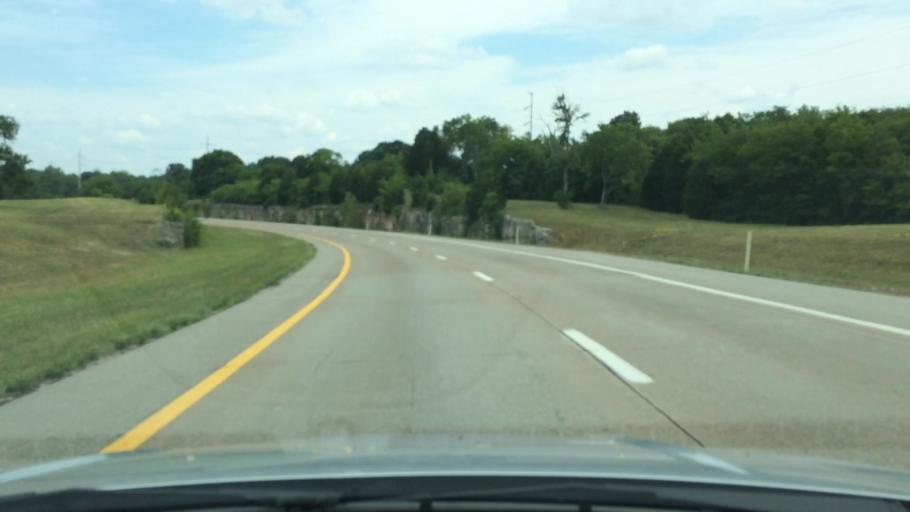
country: US
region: Tennessee
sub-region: Maury County
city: Spring Hill
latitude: 35.7403
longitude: -86.8698
